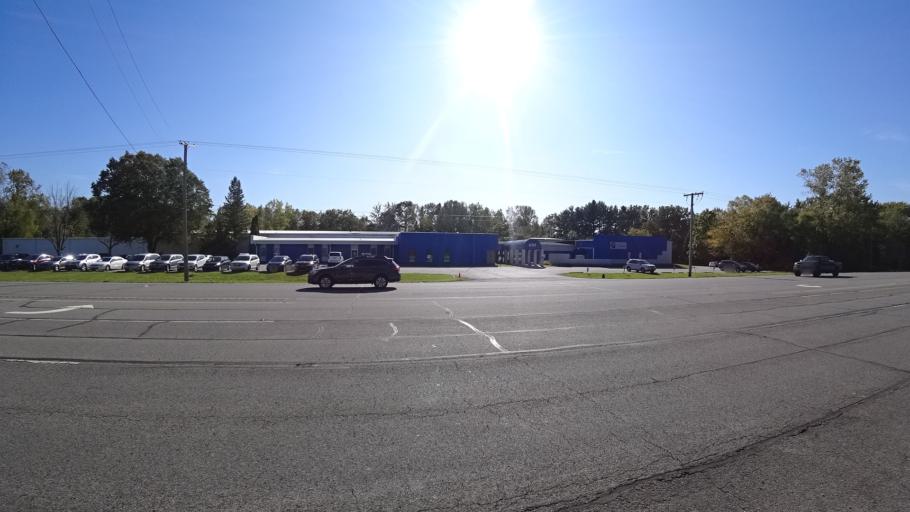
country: US
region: Indiana
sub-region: LaPorte County
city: Trail Creek
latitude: 41.7009
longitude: -86.8381
